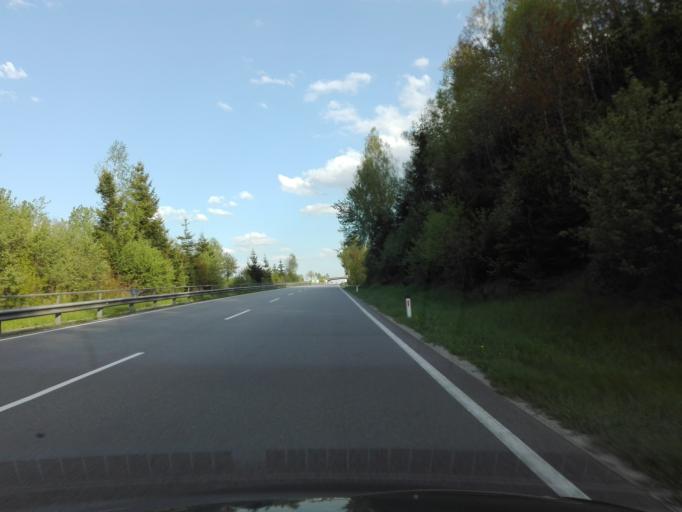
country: AT
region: Upper Austria
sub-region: Politischer Bezirk Rohrbach
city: Kleinzell im Muehlkreis
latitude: 48.4753
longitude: 13.9986
